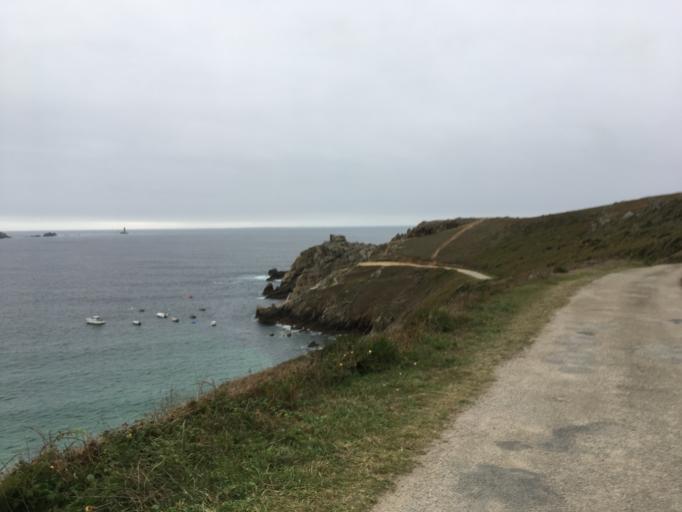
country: FR
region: Brittany
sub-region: Departement du Finistere
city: Plogoff
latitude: 48.0532
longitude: -4.7095
